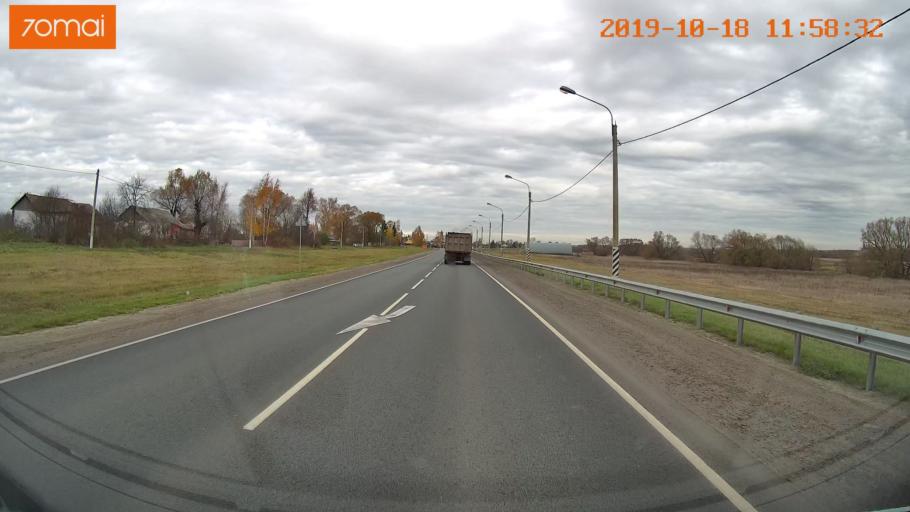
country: RU
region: Rjazan
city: Zakharovo
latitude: 54.2727
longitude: 39.1681
